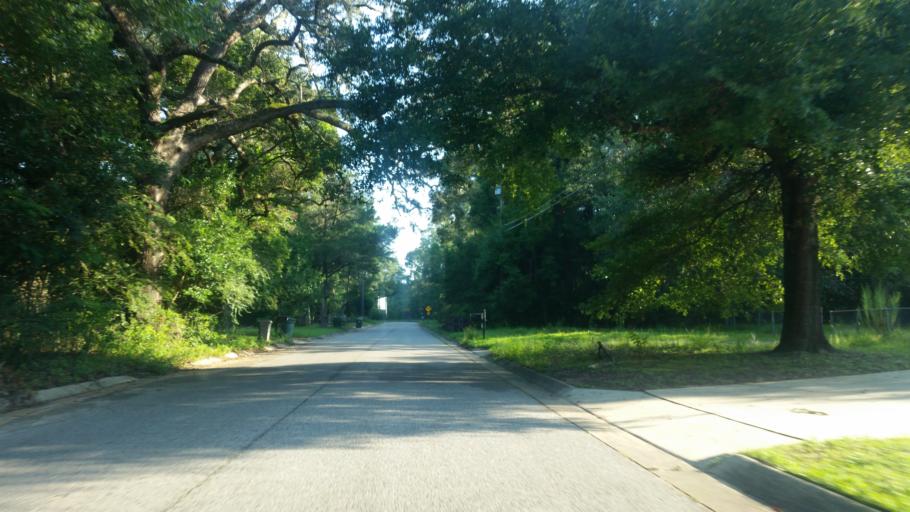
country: US
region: Florida
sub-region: Escambia County
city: Ensley
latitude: 30.5236
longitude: -87.3219
